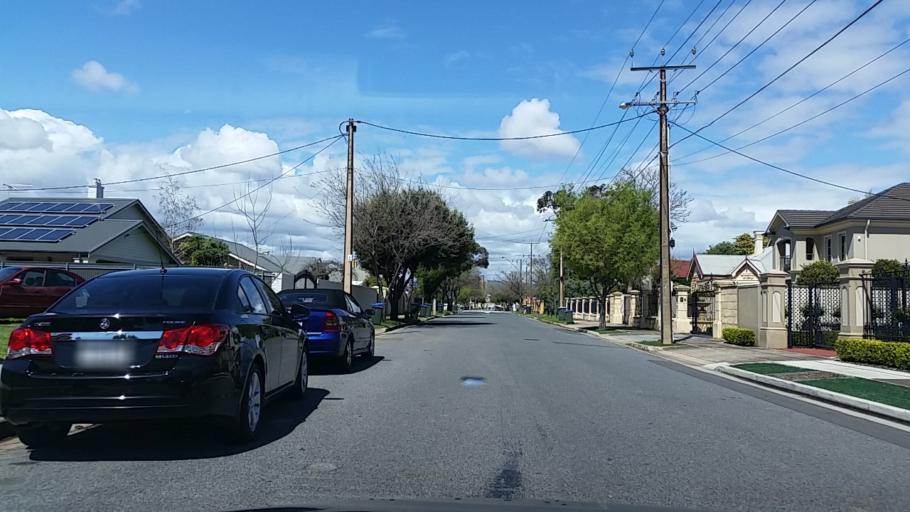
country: AU
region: South Australia
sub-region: Charles Sturt
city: Woodville North
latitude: -34.8777
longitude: 138.5442
